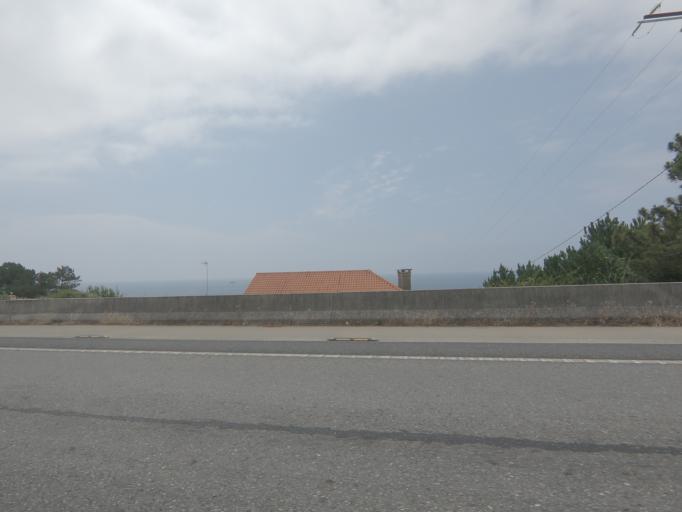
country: ES
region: Galicia
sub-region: Provincia de Pontevedra
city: Oia
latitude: 41.9697
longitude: -8.8839
